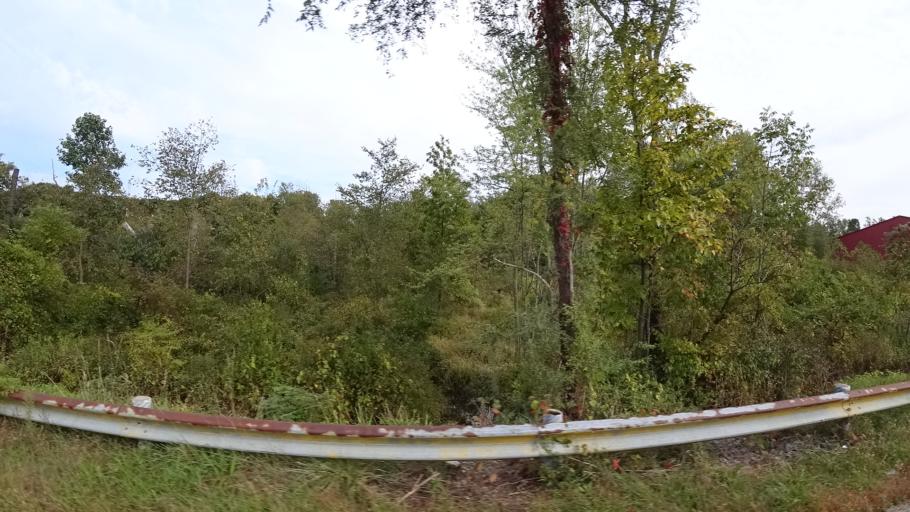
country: US
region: Indiana
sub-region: LaPorte County
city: Trail Creek
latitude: 41.7115
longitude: -86.8163
